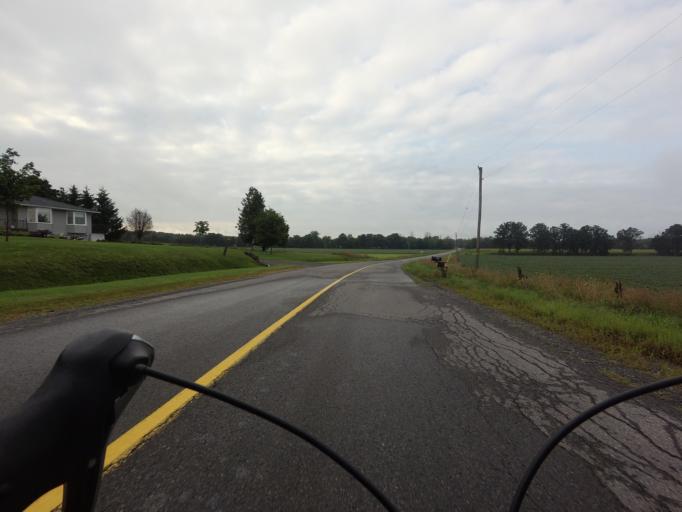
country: CA
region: Ontario
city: Bells Corners
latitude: 45.2602
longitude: -75.8095
